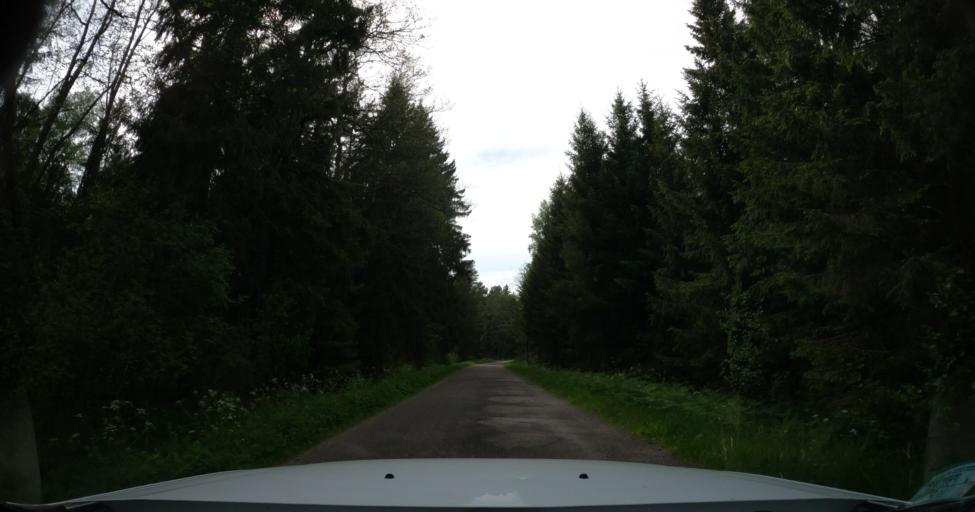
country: PL
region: Warmian-Masurian Voivodeship
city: Dobre Miasto
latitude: 54.0960
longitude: 20.3914
